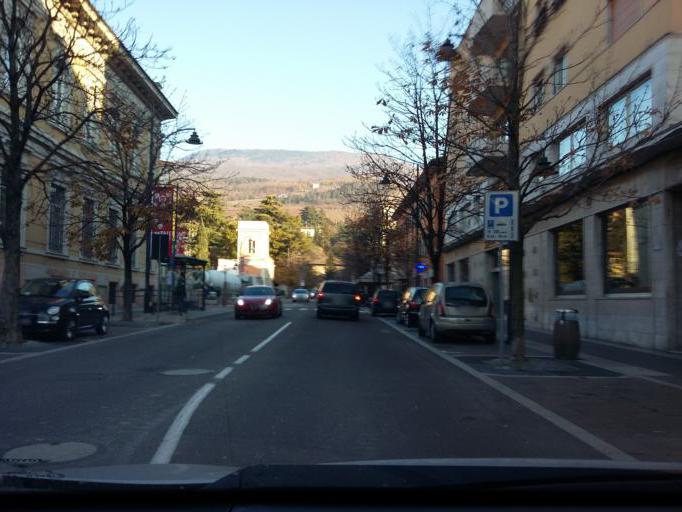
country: IT
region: Trentino-Alto Adige
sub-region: Provincia di Trento
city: Rovereto
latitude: 45.8909
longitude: 11.0405
